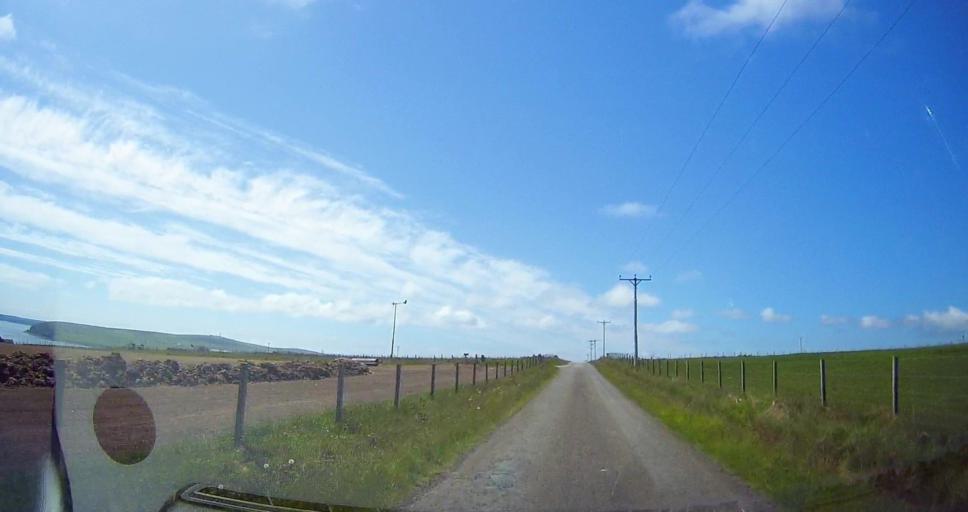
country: GB
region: Scotland
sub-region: Orkney Islands
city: Kirkwall
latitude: 58.8146
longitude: -2.9188
